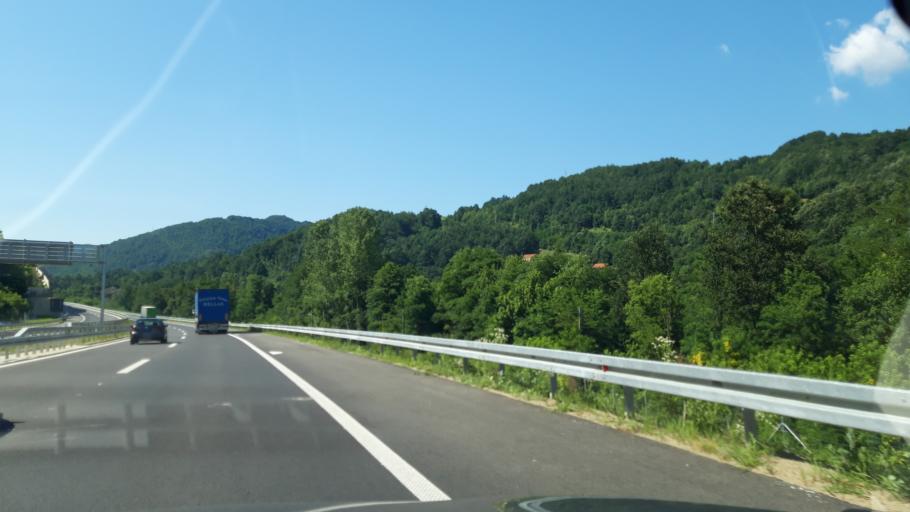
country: RS
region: Central Serbia
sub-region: Jablanicki Okrug
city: Vlasotince
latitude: 42.8490
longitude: 22.1294
